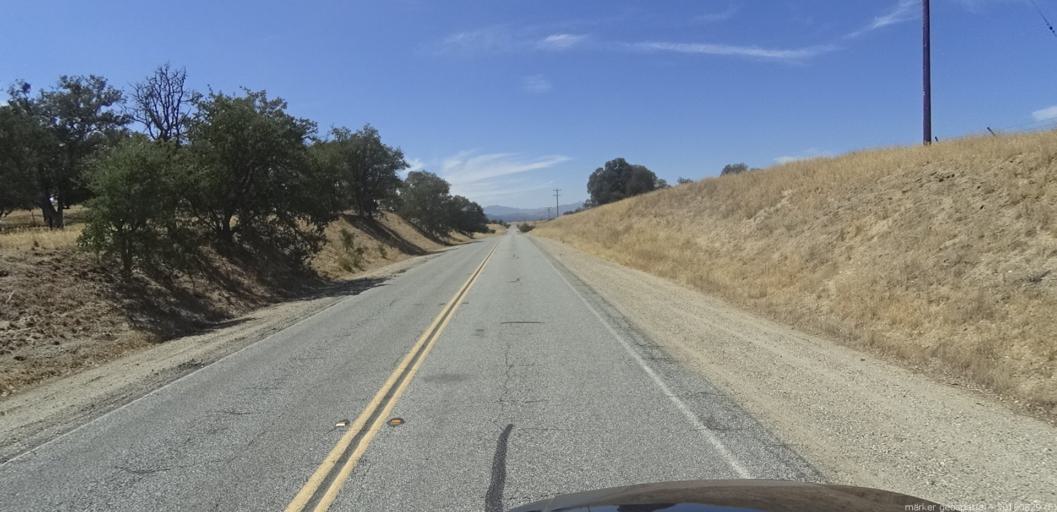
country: US
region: California
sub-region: Monterey County
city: King City
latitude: 35.9384
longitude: -121.1107
